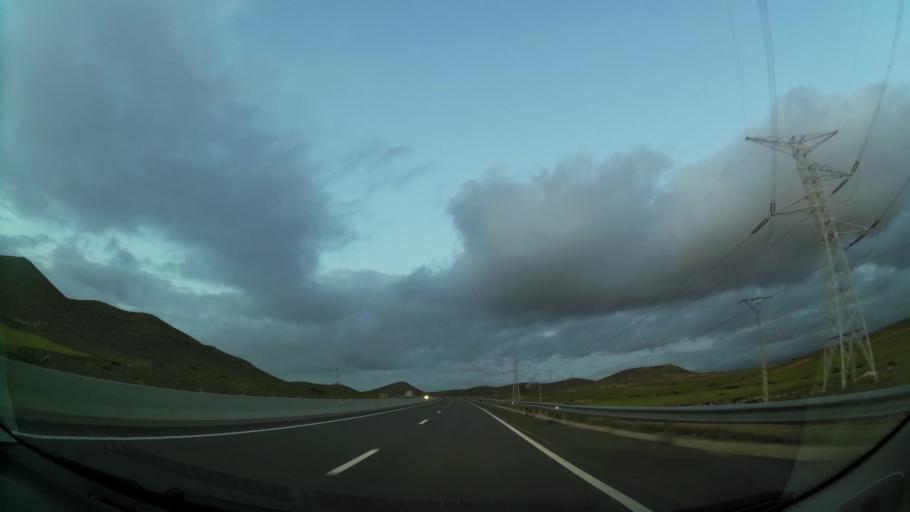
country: MA
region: Oriental
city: El Aioun
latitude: 34.6142
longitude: -2.4285
